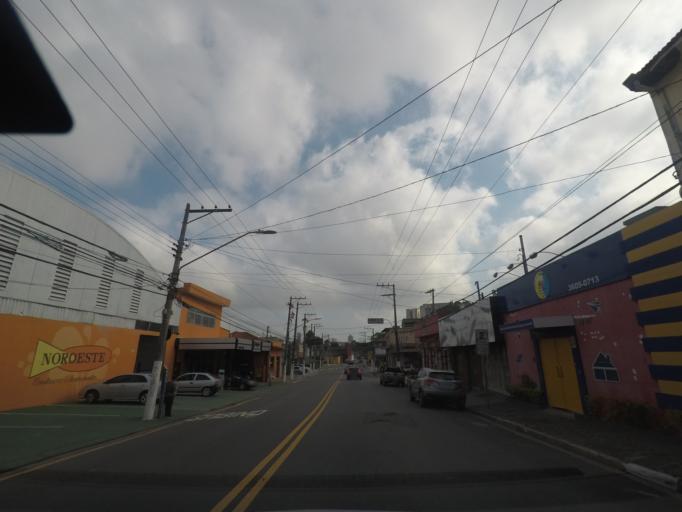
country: BR
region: Sao Paulo
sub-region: Osasco
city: Osasco
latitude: -23.5592
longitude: -46.7818
